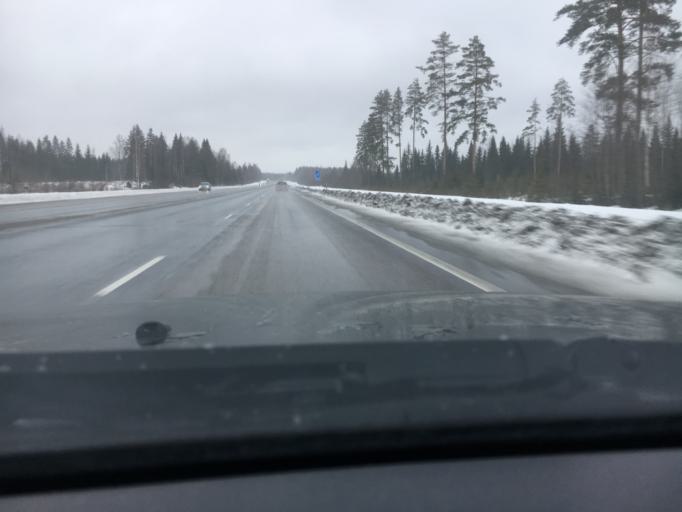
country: FI
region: Central Finland
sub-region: Joutsa
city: Joutsa
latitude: 61.7712
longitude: 26.1010
